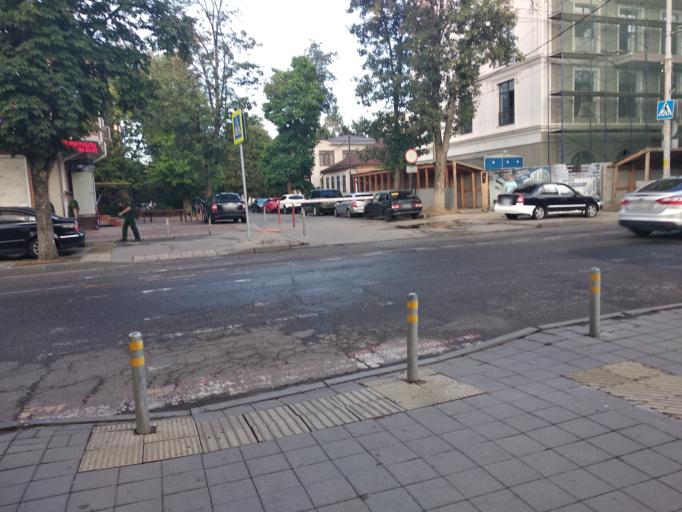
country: RU
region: Krasnodarskiy
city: Krasnodar
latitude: 45.0170
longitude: 38.9633
